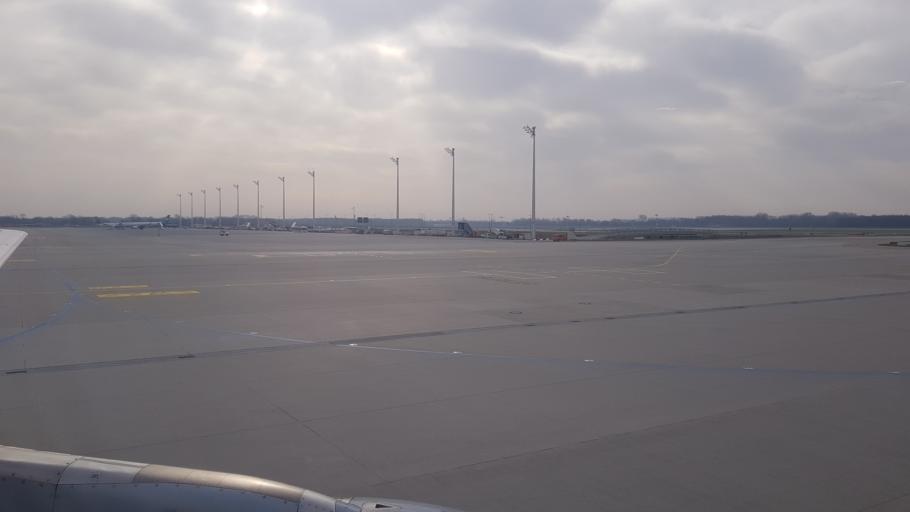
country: DE
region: Bavaria
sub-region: Upper Bavaria
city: Hallbergmoos
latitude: 48.3507
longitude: 11.7953
